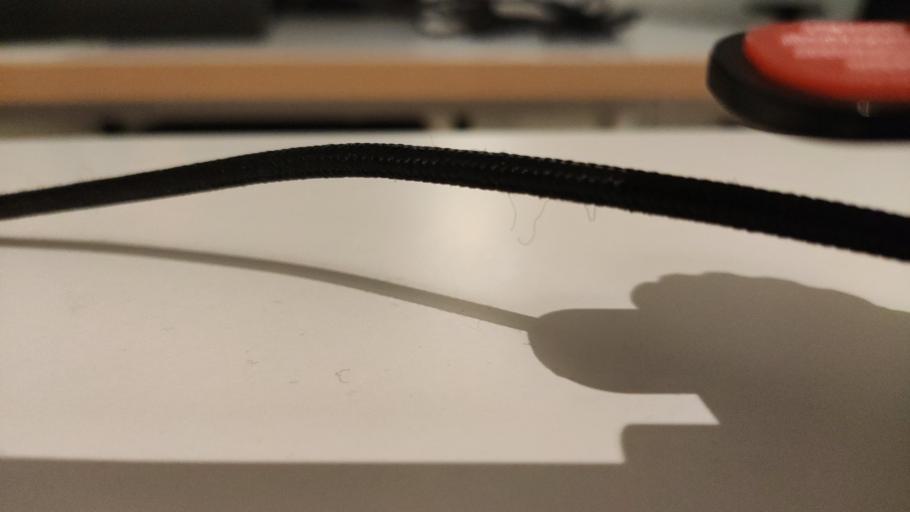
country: RU
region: Moskovskaya
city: Novosin'kovo
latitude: 56.3776
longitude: 37.3280
